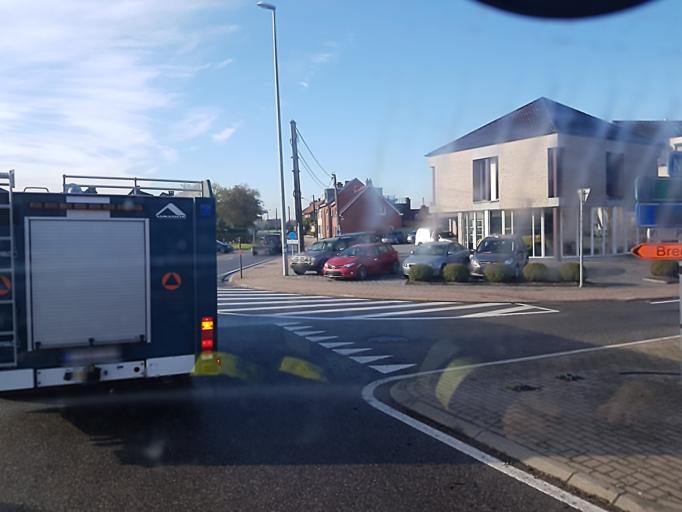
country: BE
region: Flanders
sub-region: Provincie Antwerpen
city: Brecht
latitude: 51.3479
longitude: 4.6699
